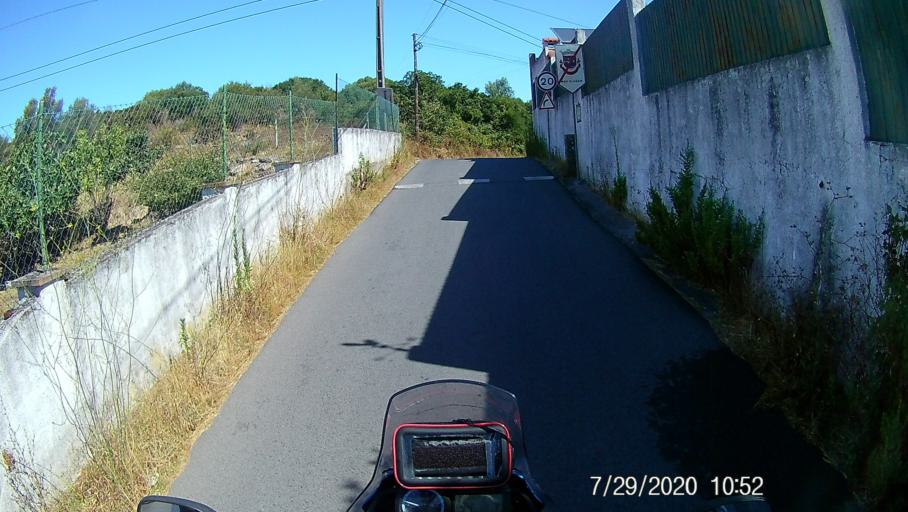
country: PT
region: Lisbon
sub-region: Cascais
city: Alcabideche
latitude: 38.7467
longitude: -9.3699
